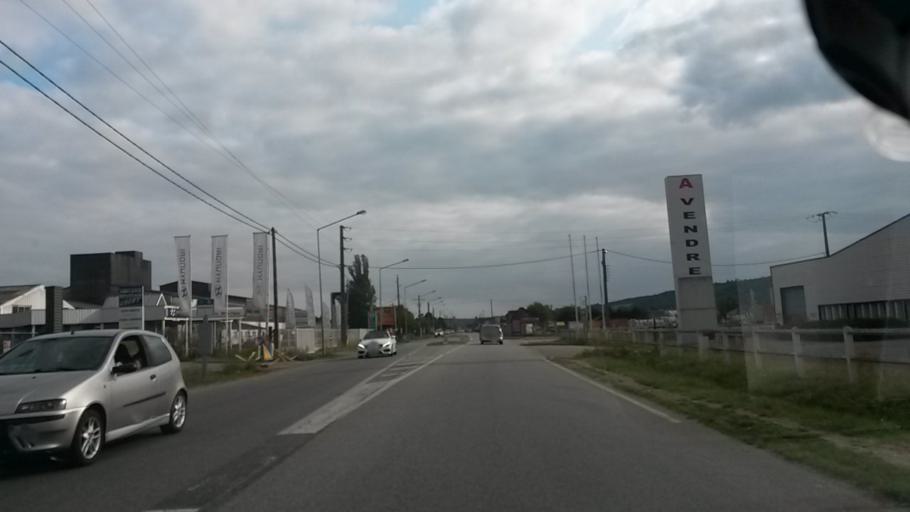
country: FR
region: Haute-Normandie
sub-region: Departement de l'Eure
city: Gravigny
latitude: 49.0572
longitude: 1.1685
